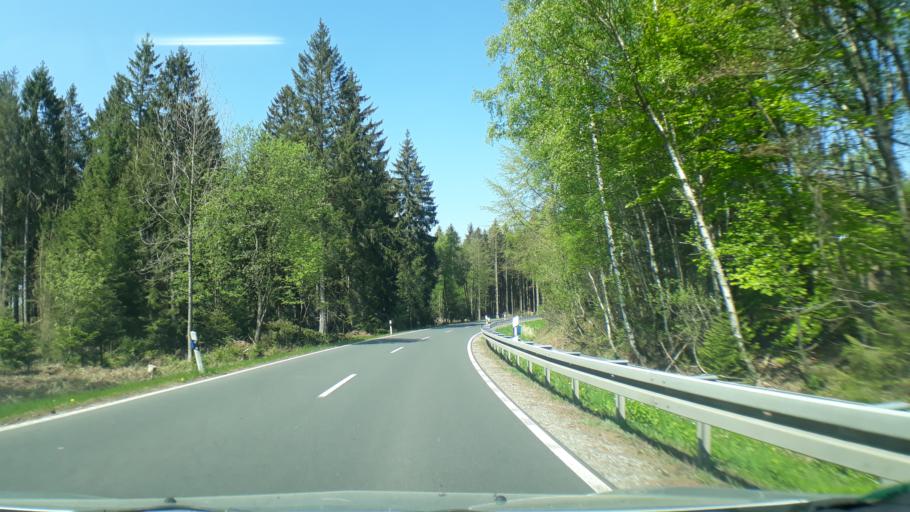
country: DE
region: North Rhine-Westphalia
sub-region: Regierungsbezirk Koln
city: Roetgen
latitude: 50.6477
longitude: 6.2594
